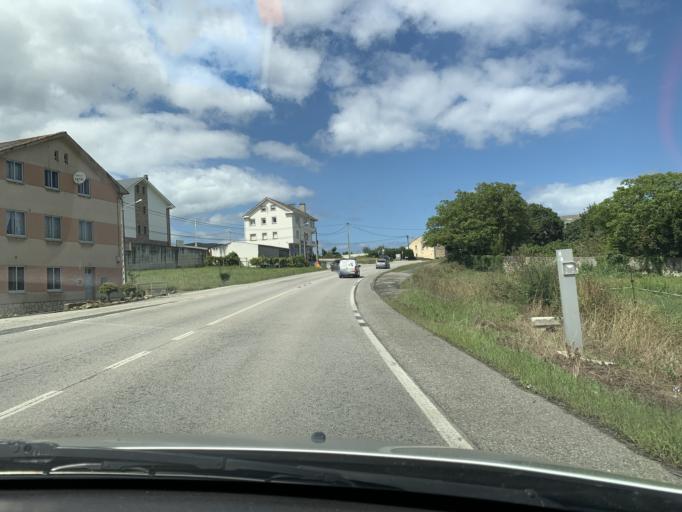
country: ES
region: Galicia
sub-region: Provincia de Lugo
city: Foz
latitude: 43.5562
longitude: -7.2702
